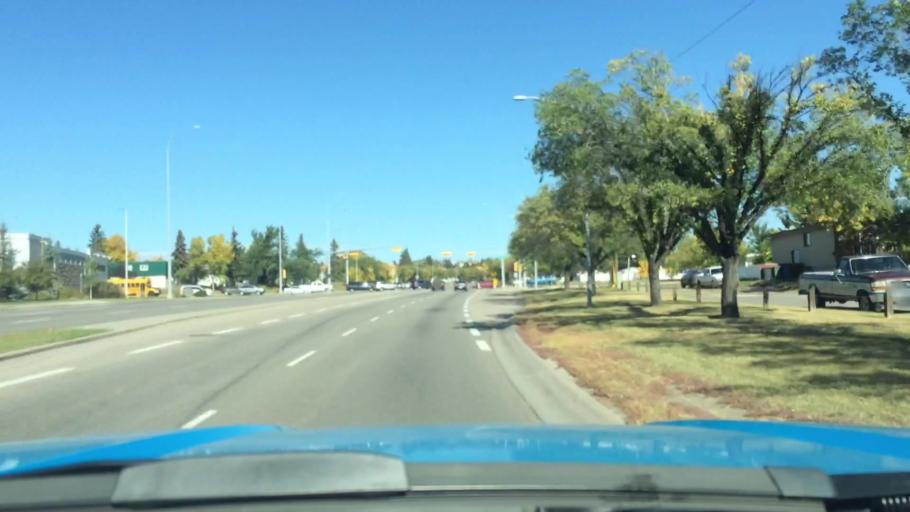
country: CA
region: Alberta
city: Calgary
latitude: 51.1169
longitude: -114.0686
